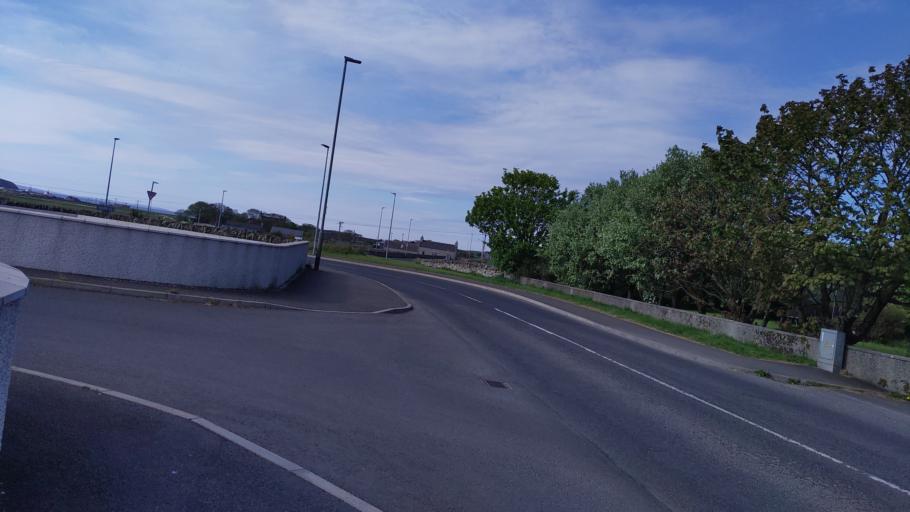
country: GB
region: Scotland
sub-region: Orkney Islands
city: Orkney
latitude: 58.9748
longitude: -2.9705
